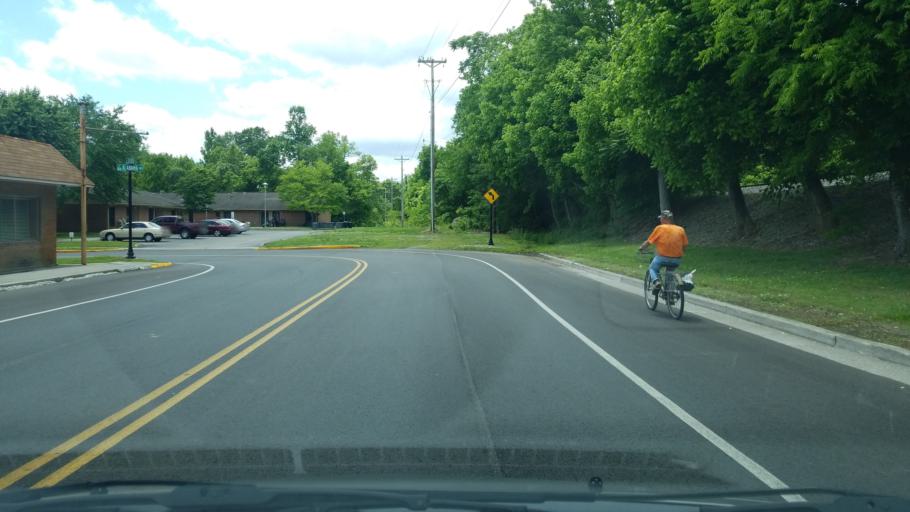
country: US
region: Tennessee
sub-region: Rhea County
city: Dayton
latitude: 35.4931
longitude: -85.0164
